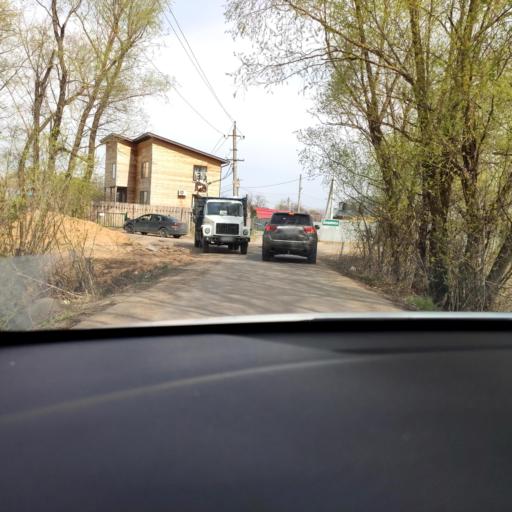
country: RU
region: Tatarstan
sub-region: Gorod Kazan'
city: Kazan
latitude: 55.8492
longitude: 49.1647
